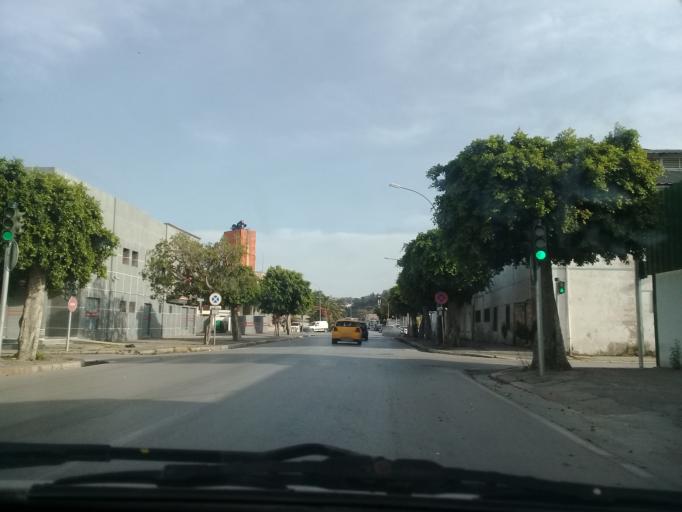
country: TN
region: Tunis
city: Tunis
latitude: 36.7950
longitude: 10.1870
